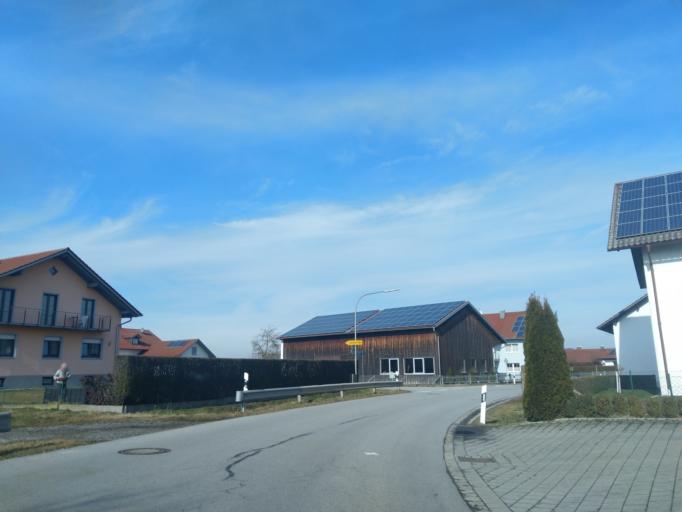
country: DE
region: Bavaria
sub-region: Lower Bavaria
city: Buchhofen
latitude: 48.6684
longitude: 12.9634
